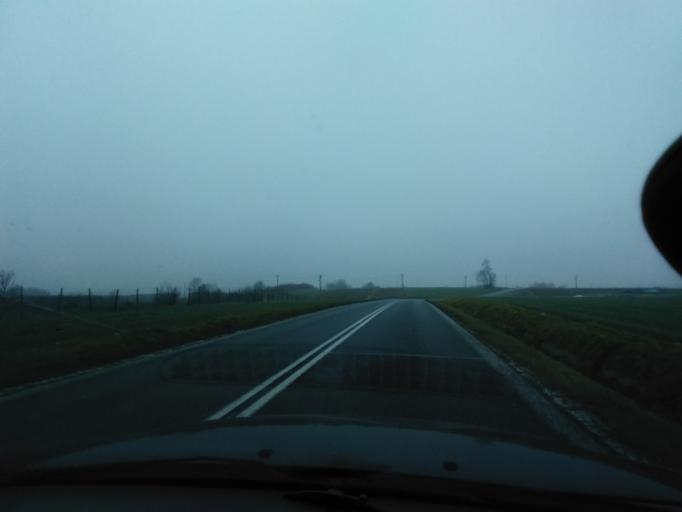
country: PL
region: Subcarpathian Voivodeship
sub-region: Powiat lancucki
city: Sonina
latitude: 50.0517
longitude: 22.2862
